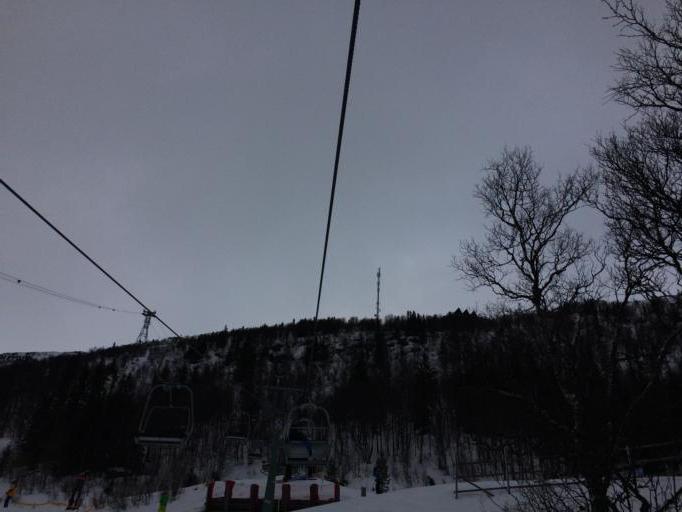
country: SE
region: Jaemtland
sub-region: Are Kommun
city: Are
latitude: 63.4087
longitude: 13.0791
